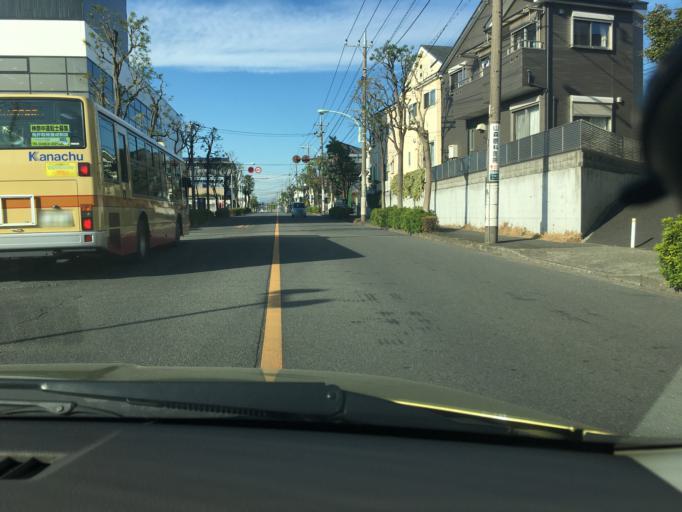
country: JP
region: Tokyo
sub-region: Machida-shi
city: Machida
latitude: 35.5650
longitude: 139.4198
